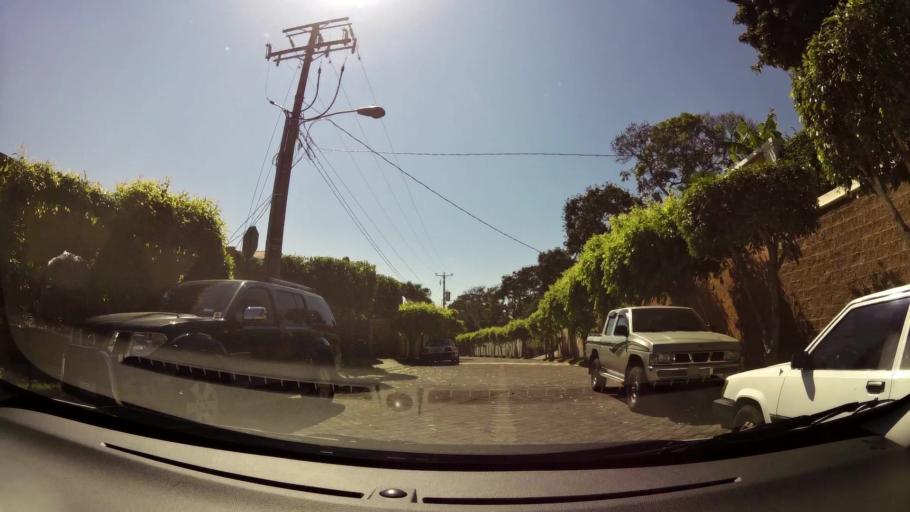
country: SV
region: La Libertad
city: Santa Tecla
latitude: 13.6584
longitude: -89.2826
